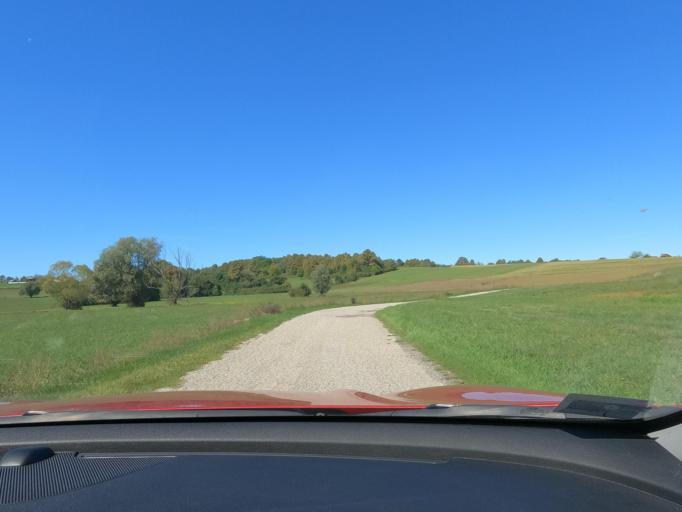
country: HR
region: Sisacko-Moslavacka
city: Petrinja
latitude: 45.3334
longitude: 16.2160
